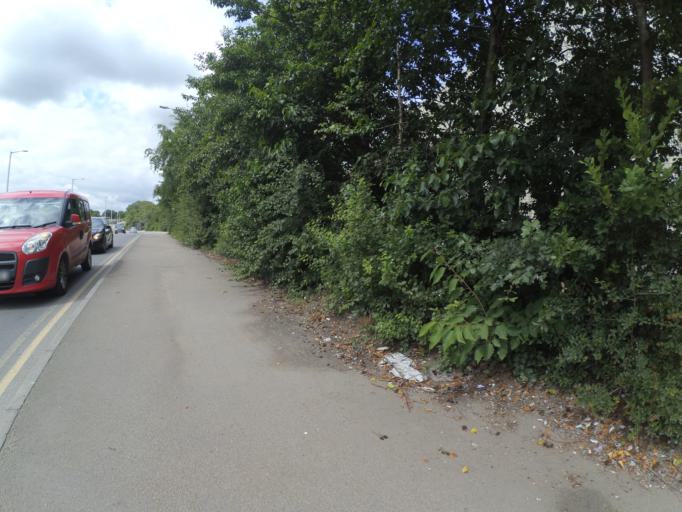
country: GB
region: England
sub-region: Warwickshire
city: Rugby
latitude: 52.3755
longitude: -1.2836
